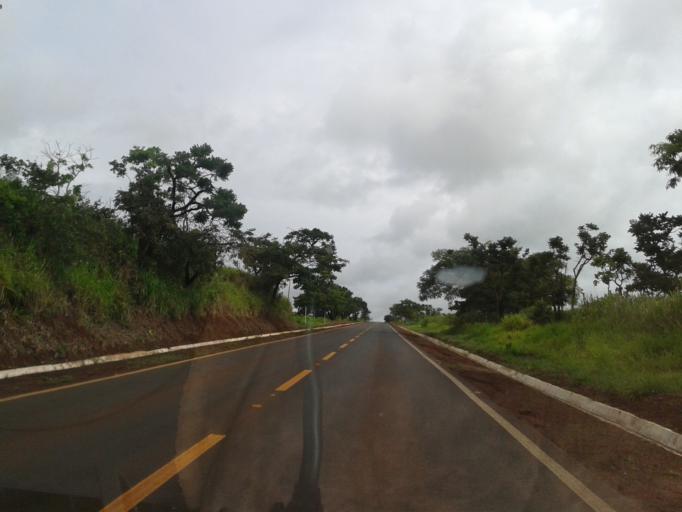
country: BR
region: Minas Gerais
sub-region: Ituiutaba
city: Ituiutaba
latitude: -18.9343
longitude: -49.4450
